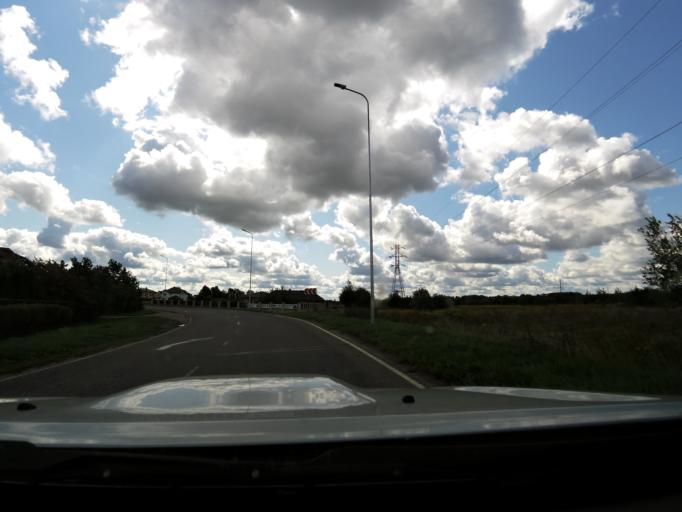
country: LV
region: Daugavpils
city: Daugavpils
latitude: 55.8657
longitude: 26.4922
